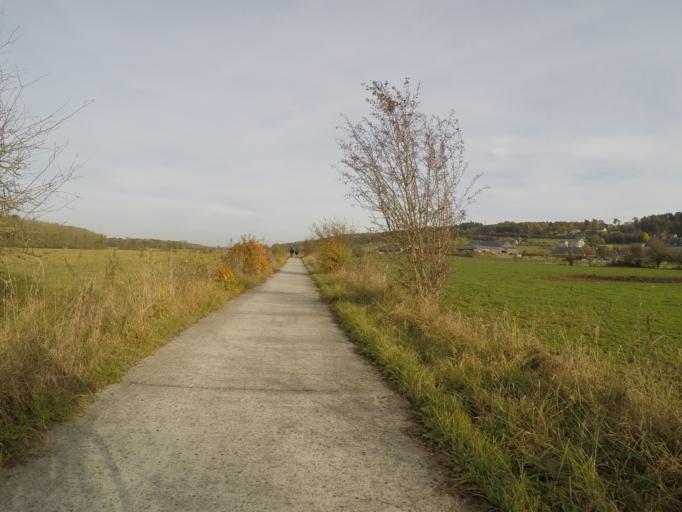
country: BE
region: Wallonia
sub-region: Province du Luxembourg
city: Marche-en-Famenne
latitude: 50.2495
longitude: 5.3939
